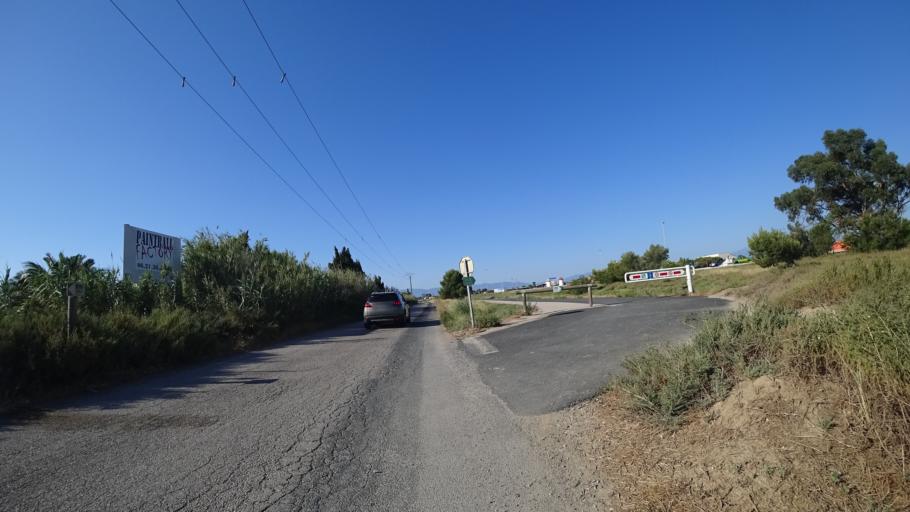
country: FR
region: Languedoc-Roussillon
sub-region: Departement des Pyrenees-Orientales
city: Torreilles
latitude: 42.7619
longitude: 3.0203
